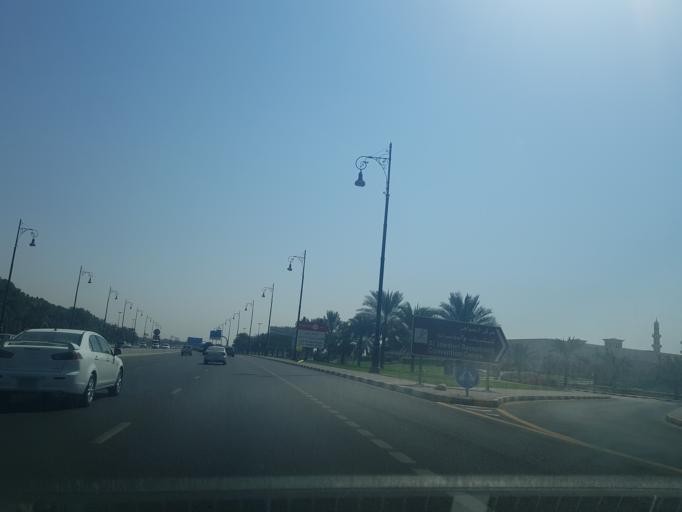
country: AE
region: Ash Shariqah
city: Sharjah
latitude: 25.3187
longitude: 55.5120
